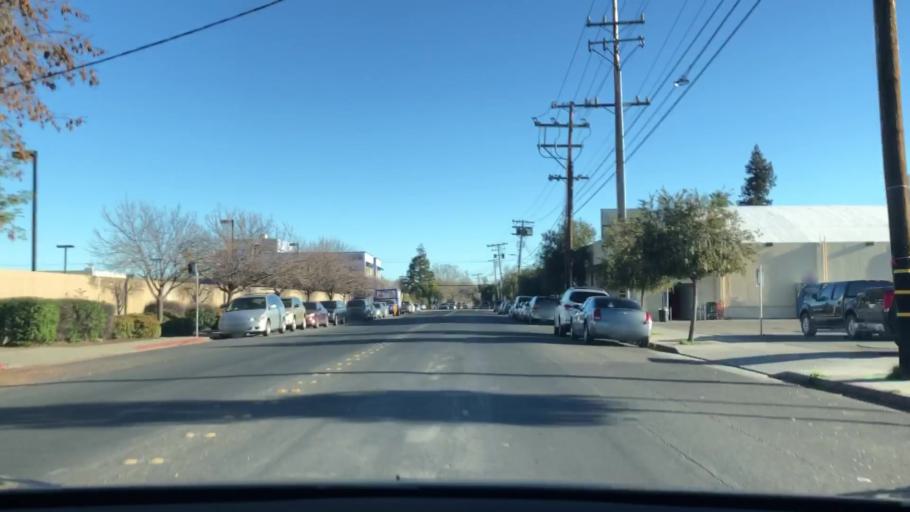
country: US
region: California
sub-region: San Mateo County
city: North Fair Oaks
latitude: 37.4799
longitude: -122.1996
